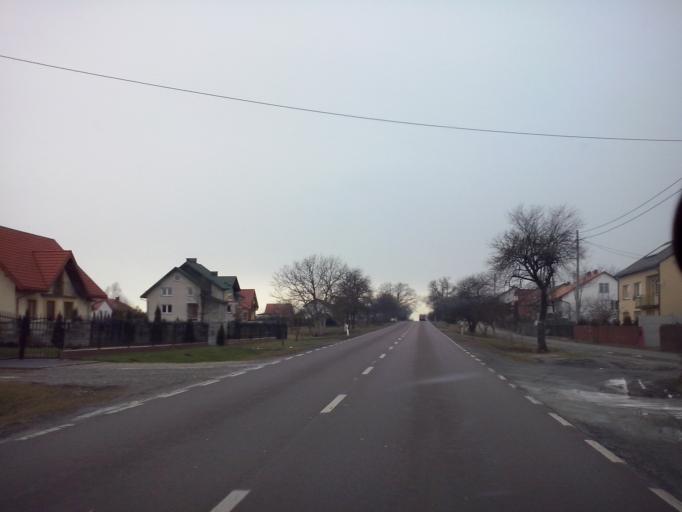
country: PL
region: Lublin Voivodeship
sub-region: Powiat bilgorajski
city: Tereszpol
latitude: 50.5868
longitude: 22.8216
